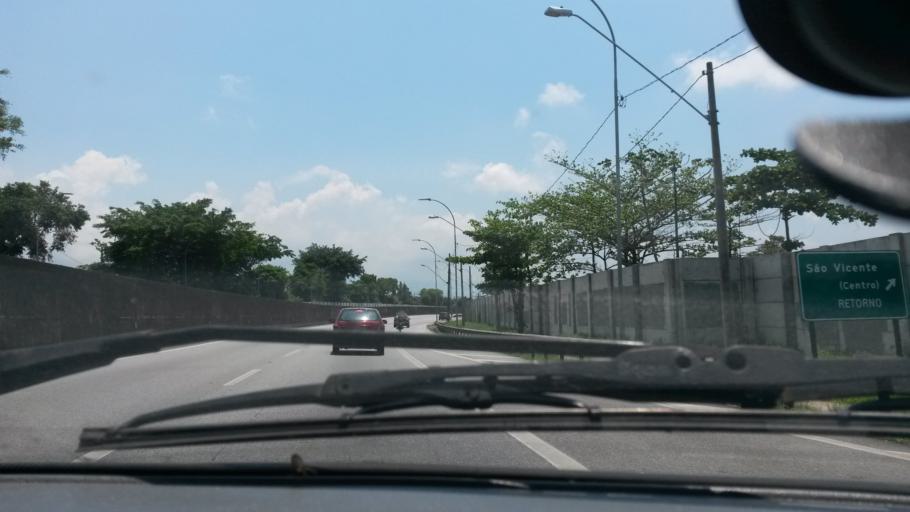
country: BR
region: Sao Paulo
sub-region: Sao Vicente
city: Sao Vicente
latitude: -23.9743
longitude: -46.4017
